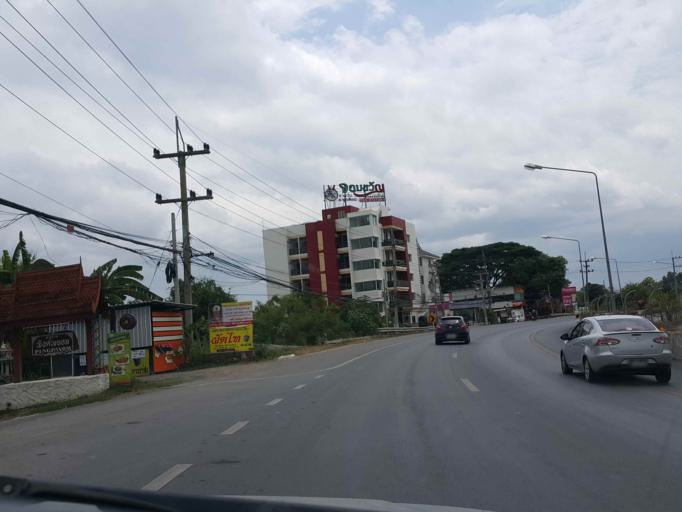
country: TH
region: Chiang Mai
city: Chiang Mai
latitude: 18.7790
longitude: 98.9581
